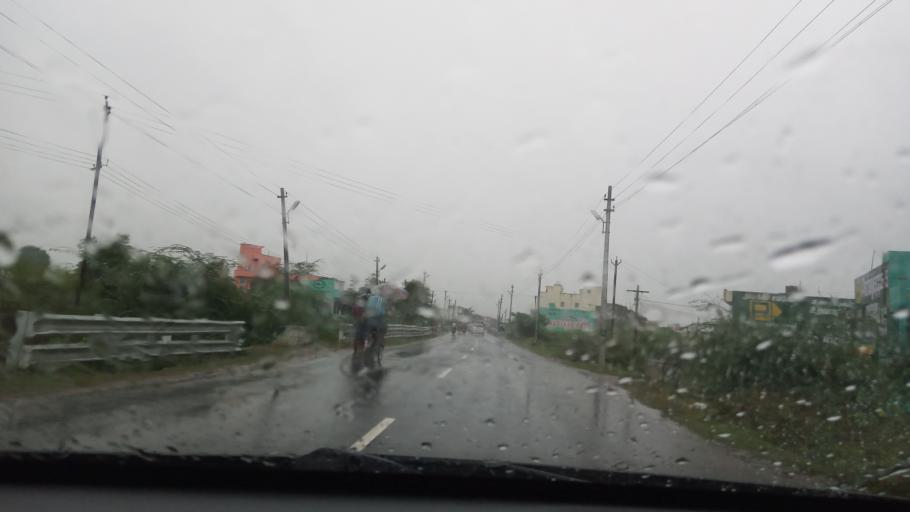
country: IN
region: Tamil Nadu
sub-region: Tiruvannamalai
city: Cheyyar
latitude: 12.6600
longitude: 79.5371
